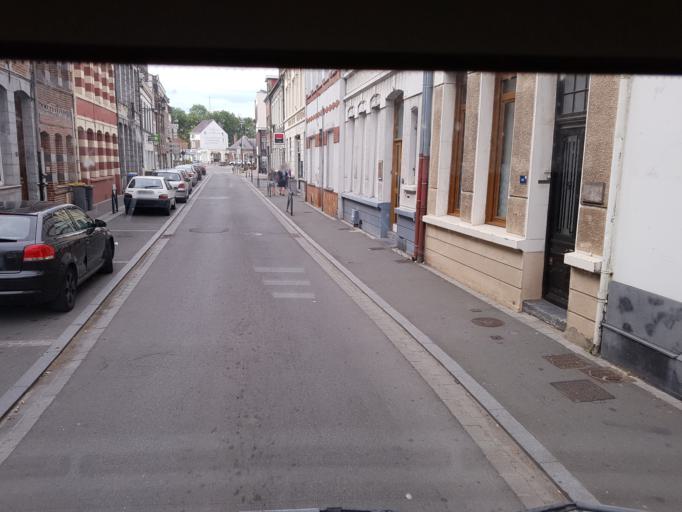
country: FR
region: Nord-Pas-de-Calais
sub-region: Departement du Nord
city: Conde-sur-l'Escaut
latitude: 50.4501
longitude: 3.5942
